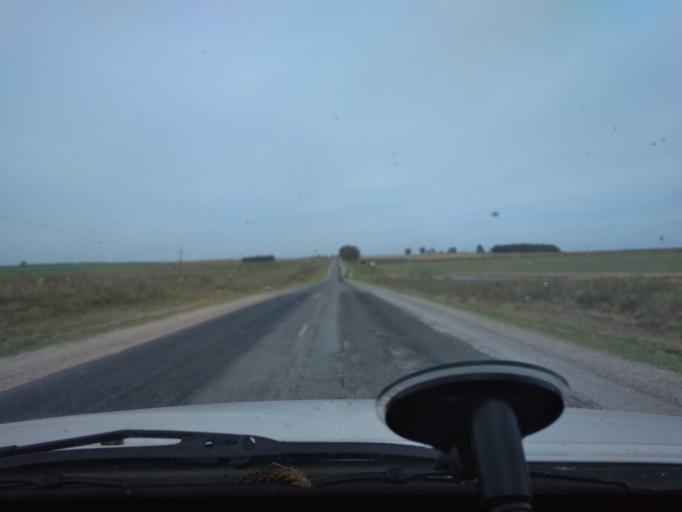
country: UY
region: Florida
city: Florida
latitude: -34.0541
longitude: -56.0187
